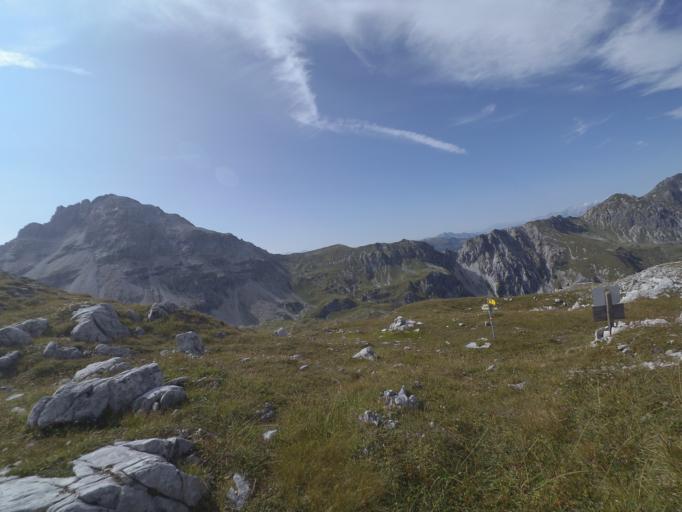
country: AT
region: Salzburg
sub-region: Politischer Bezirk Sankt Johann im Pongau
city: Kleinarl
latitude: 47.2250
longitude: 13.3890
